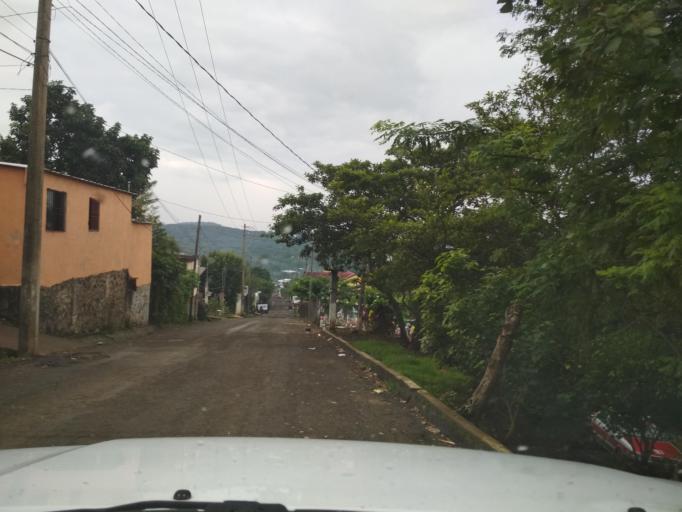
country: MX
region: Veracruz
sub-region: San Andres Tuxtla
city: San Isidro Xoteapan (San Isidro Texcaltitan)
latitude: 18.4639
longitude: -95.2347
